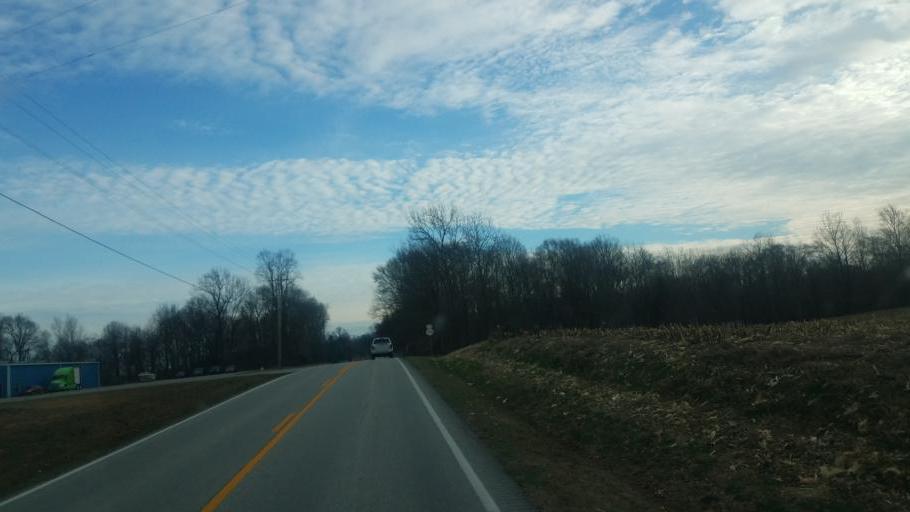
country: US
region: Kentucky
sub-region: Clinton County
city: Albany
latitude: 36.7460
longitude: -85.1262
